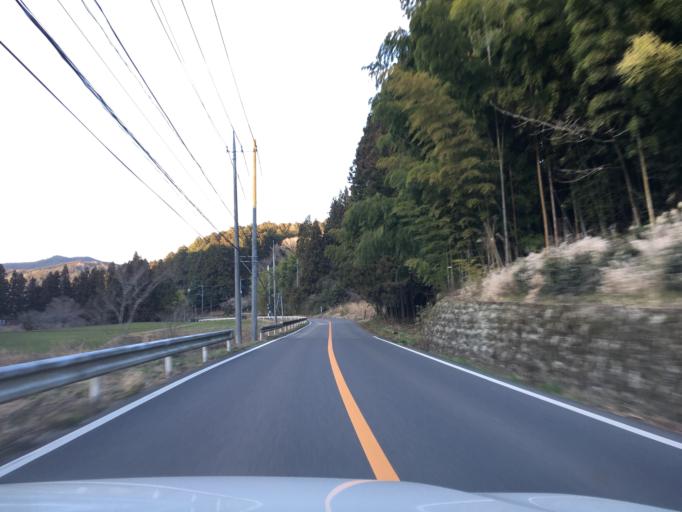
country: JP
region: Tochigi
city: Otawara
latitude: 36.8542
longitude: 140.1753
